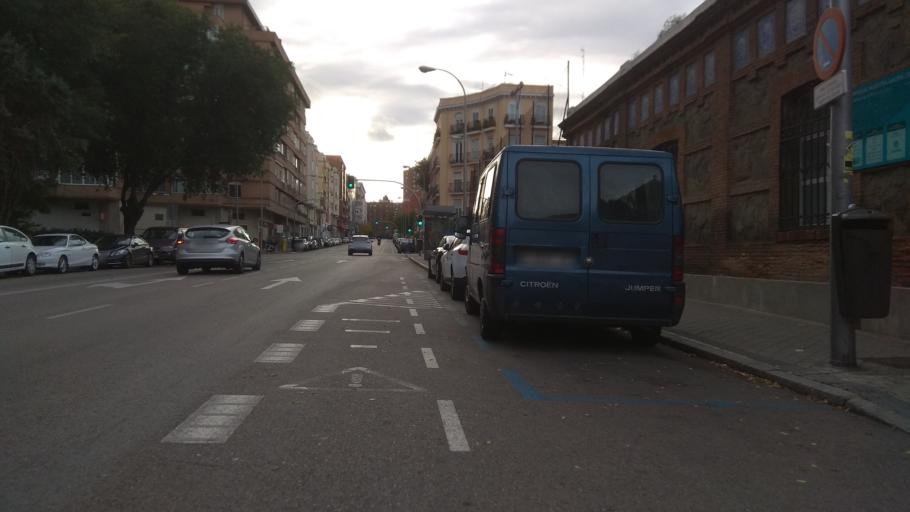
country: ES
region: Madrid
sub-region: Provincia de Madrid
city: Salamanca
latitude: 40.4325
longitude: -3.6663
